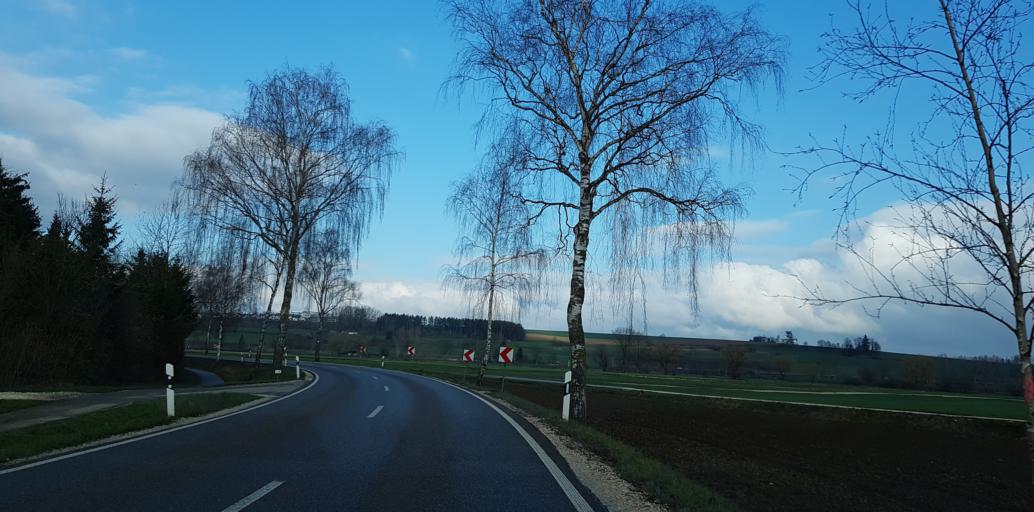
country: DE
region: Baden-Wuerttemberg
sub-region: Tuebingen Region
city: Erbach
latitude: 48.3318
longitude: 9.9172
